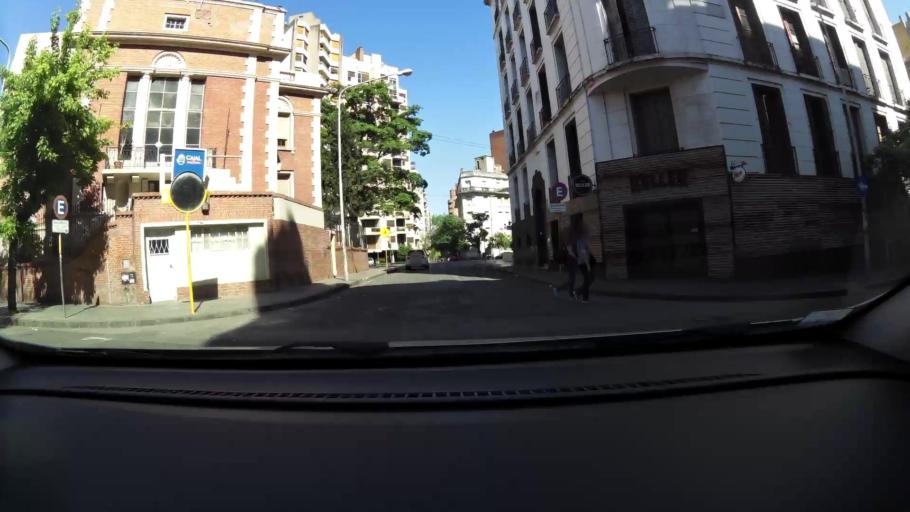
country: AR
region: Cordoba
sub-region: Departamento de Capital
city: Cordoba
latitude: -31.4263
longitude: -64.1854
